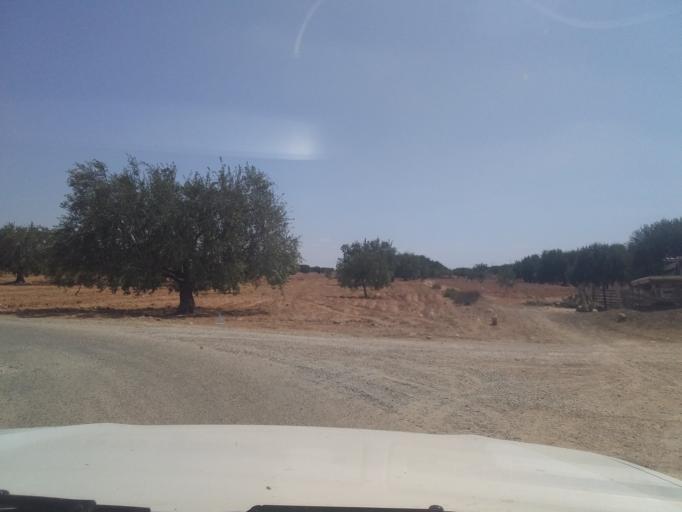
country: TN
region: Qabis
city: Matmata
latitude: 33.5906
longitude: 10.2838
